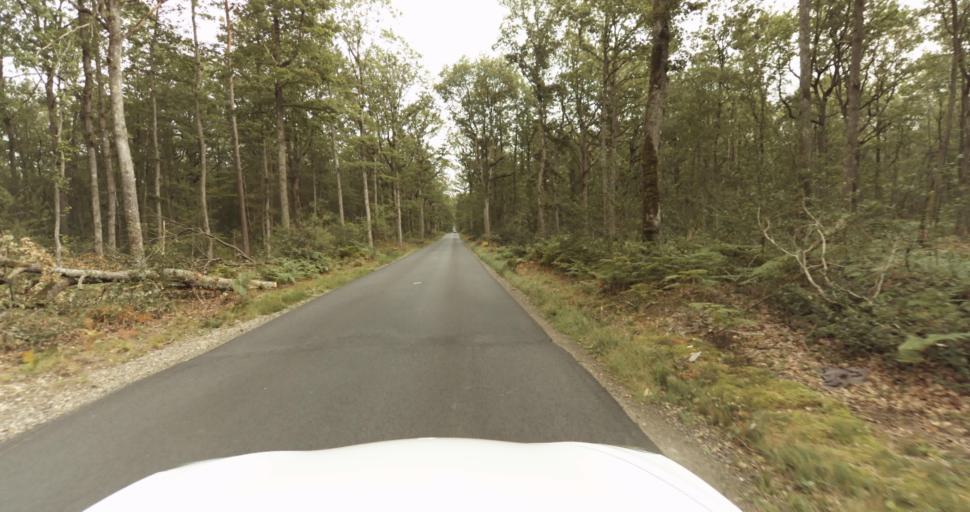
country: FR
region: Haute-Normandie
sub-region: Departement de l'Eure
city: Saint-Sebastien-de-Morsent
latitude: 48.9809
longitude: 1.0733
